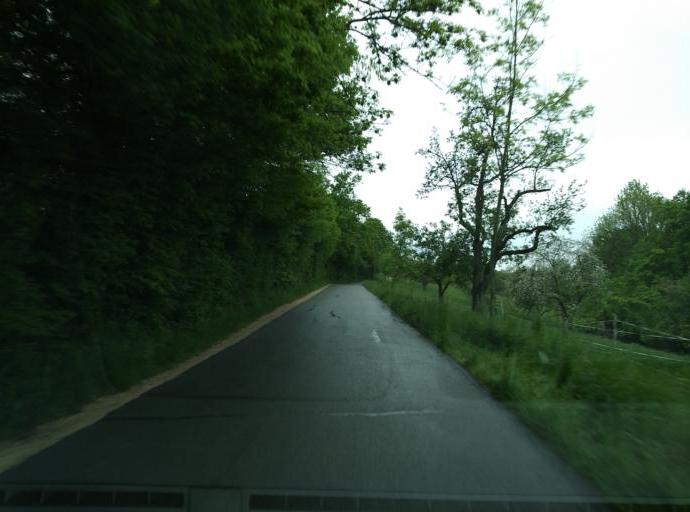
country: DE
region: Baden-Wuerttemberg
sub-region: Tuebingen Region
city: Wannweil
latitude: 48.5053
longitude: 9.1442
